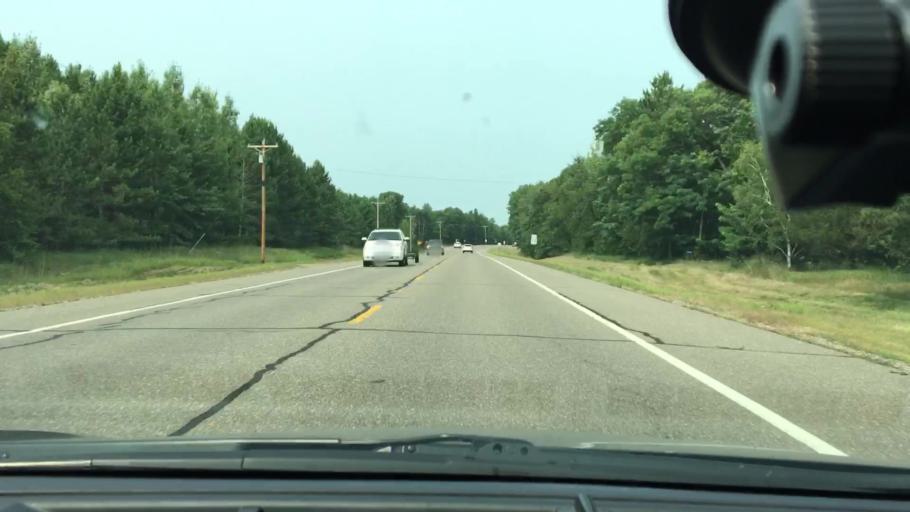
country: US
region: Minnesota
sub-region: Crow Wing County
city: Breezy Point
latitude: 46.5558
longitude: -94.1357
